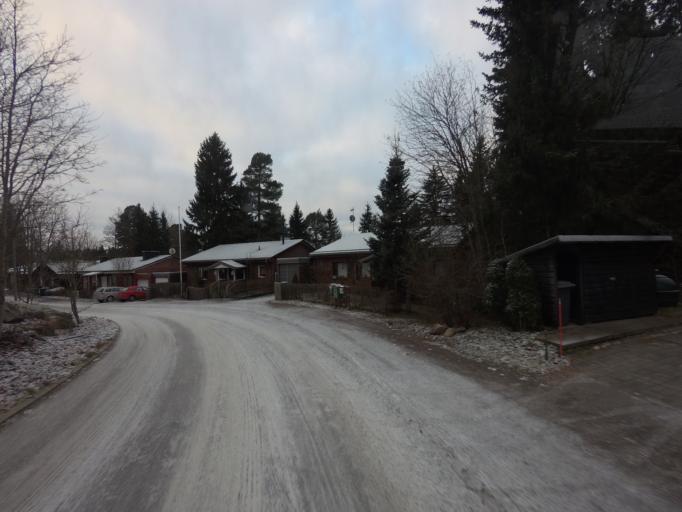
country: FI
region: Uusimaa
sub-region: Helsinki
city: Espoo
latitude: 60.1991
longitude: 24.6792
